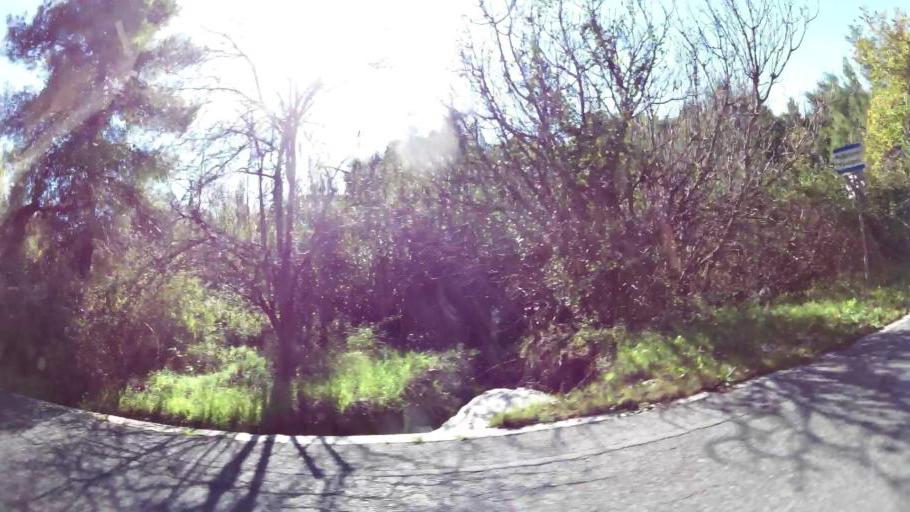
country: GR
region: Attica
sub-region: Nomarchia Anatolikis Attikis
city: Rodopoli
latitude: 38.1100
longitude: 23.8796
